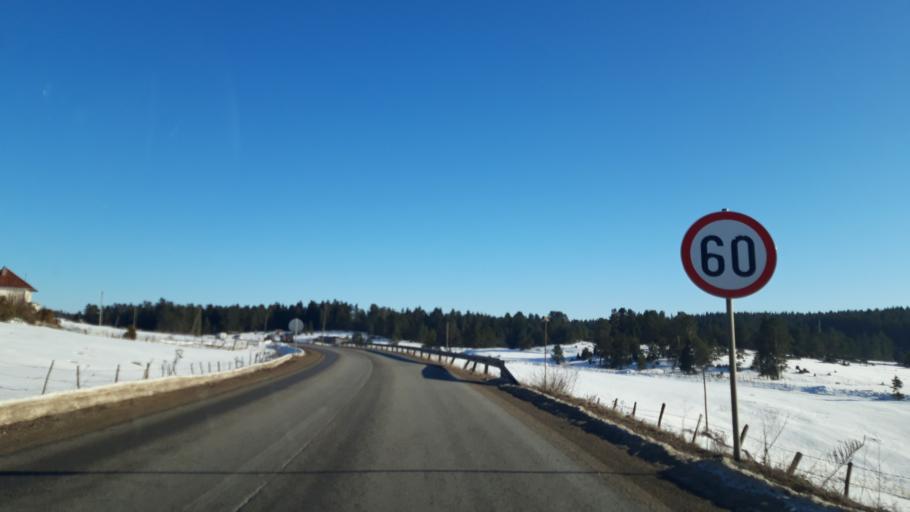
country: BA
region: Republika Srpska
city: Sokolac
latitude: 43.9200
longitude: 18.6860
